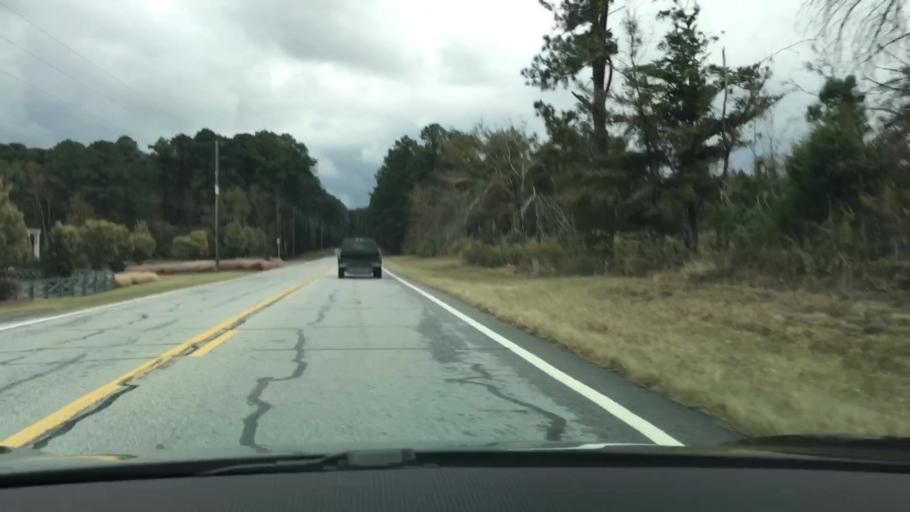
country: US
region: Georgia
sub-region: Oconee County
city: Watkinsville
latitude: 33.7860
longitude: -83.3164
